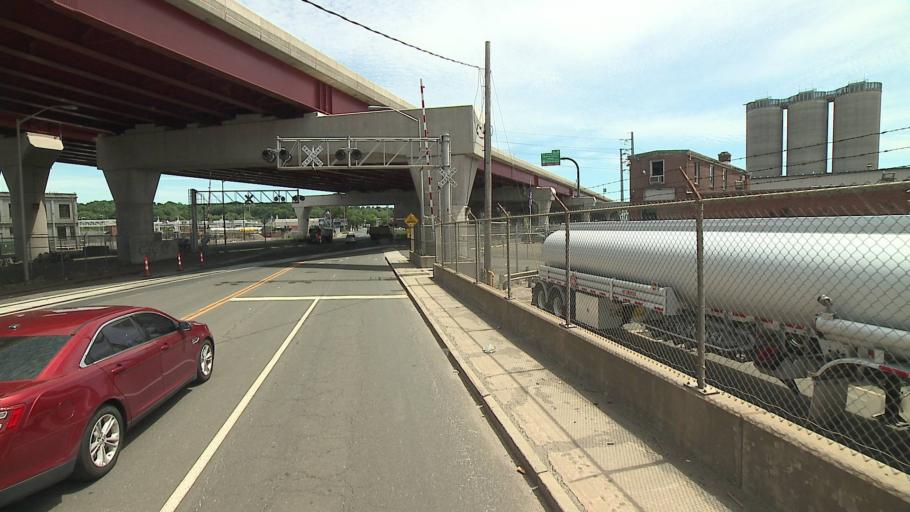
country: US
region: Connecticut
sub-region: New Haven County
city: New Haven
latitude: 41.2965
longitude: -72.9027
